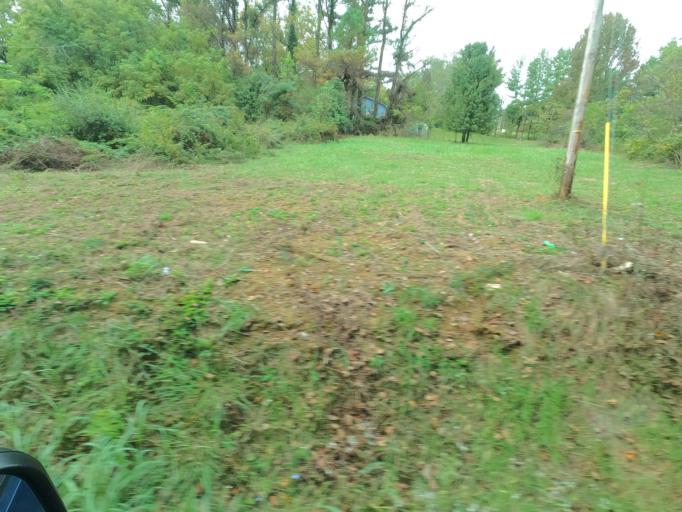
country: US
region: Tennessee
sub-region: Washington County
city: Jonesborough
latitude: 36.2719
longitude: -82.5324
